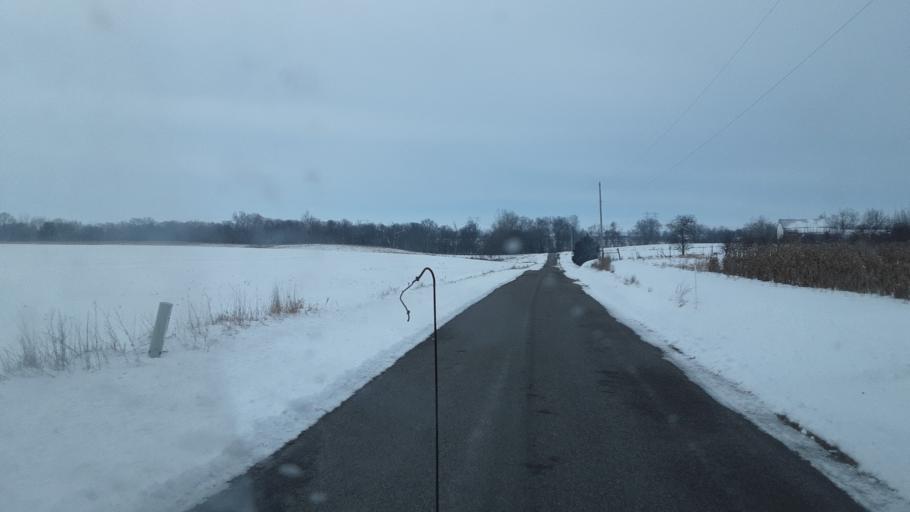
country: US
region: Ohio
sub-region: Union County
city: Marysville
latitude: 40.1737
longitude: -83.4047
